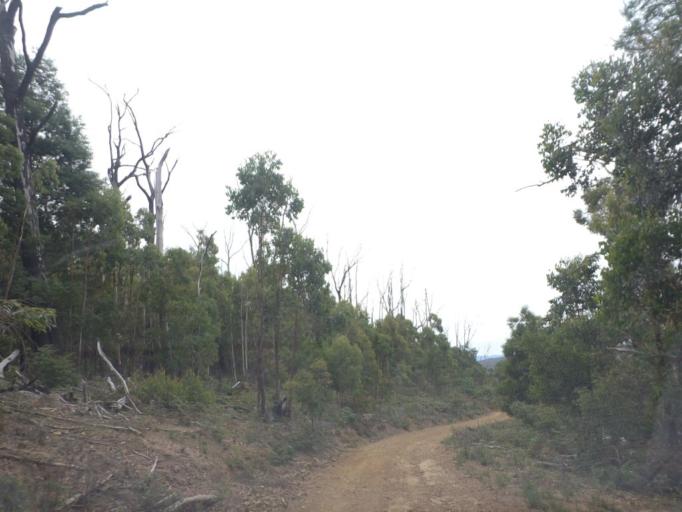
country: AU
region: Victoria
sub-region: Murrindindi
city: Alexandra
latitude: -37.3889
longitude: 145.5704
